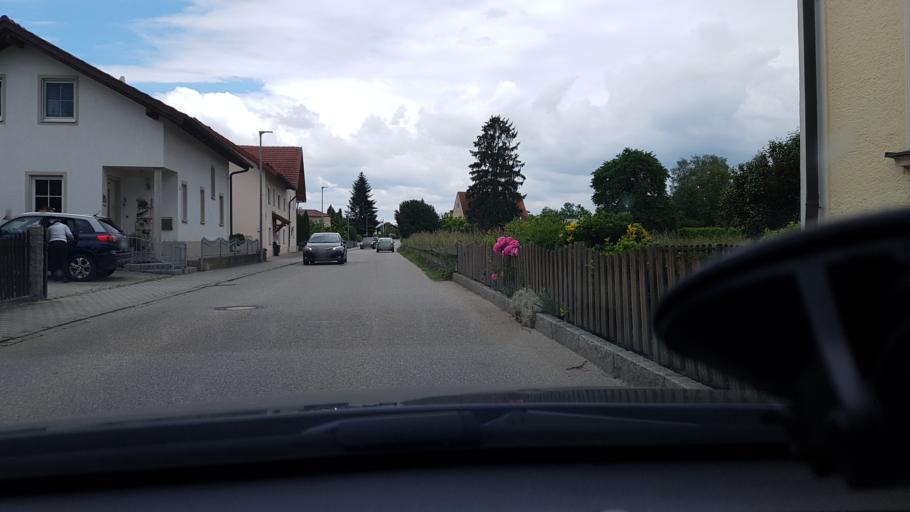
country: AT
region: Upper Austria
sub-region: Politischer Bezirk Scharding
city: Sankt Marienkirchen bei Schaerding
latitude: 48.4035
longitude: 13.3871
